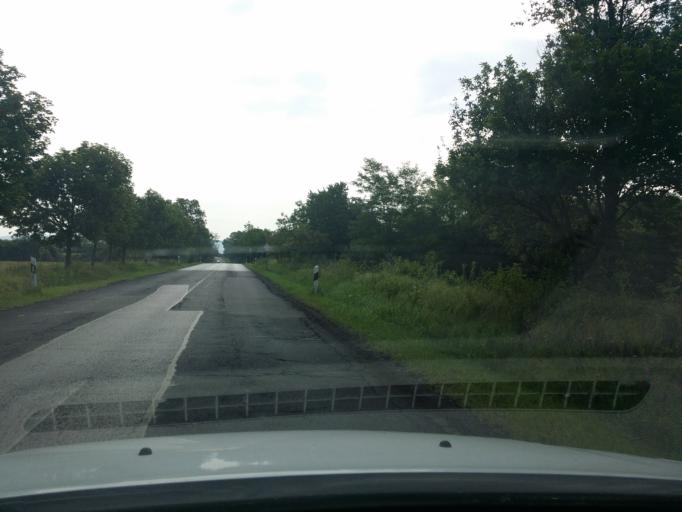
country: HU
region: Borsod-Abauj-Zemplen
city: Satoraljaujhely
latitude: 48.4717
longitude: 21.5492
